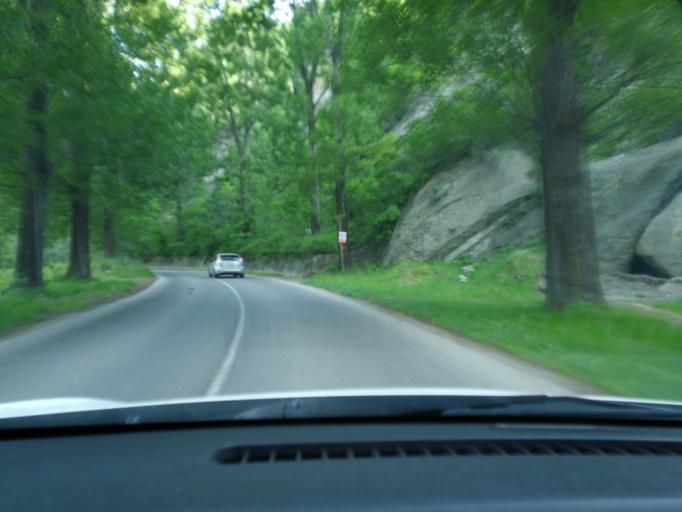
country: RO
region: Prahova
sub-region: Comuna Sotrile
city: Sotrile
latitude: 45.2074
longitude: 25.7404
